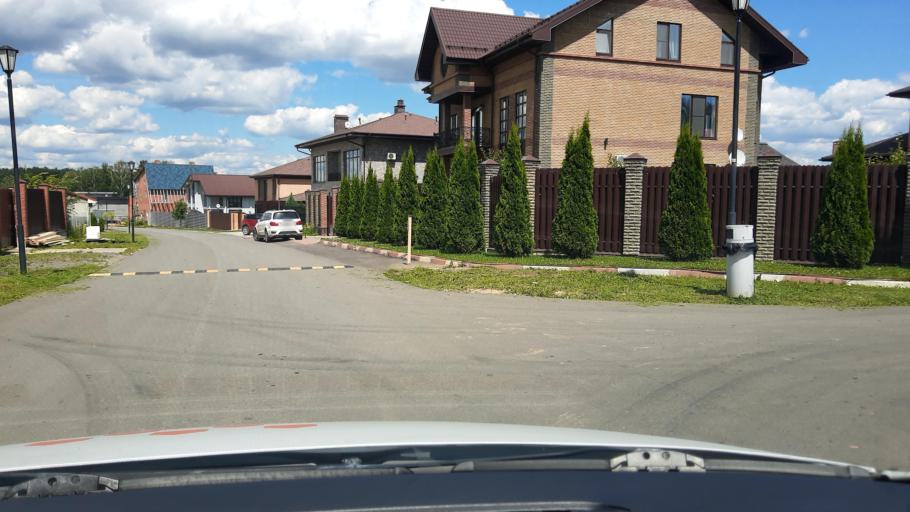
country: RU
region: Moskovskaya
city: Filimonki
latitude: 55.5443
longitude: 37.3378
